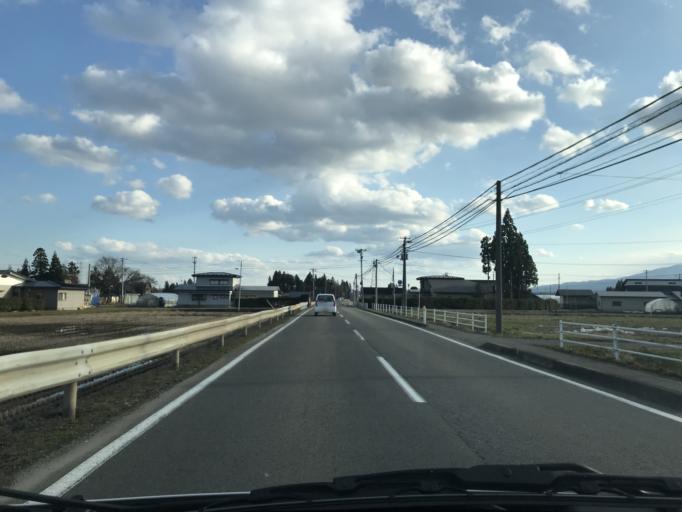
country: JP
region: Iwate
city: Kitakami
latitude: 39.3107
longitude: 141.0347
